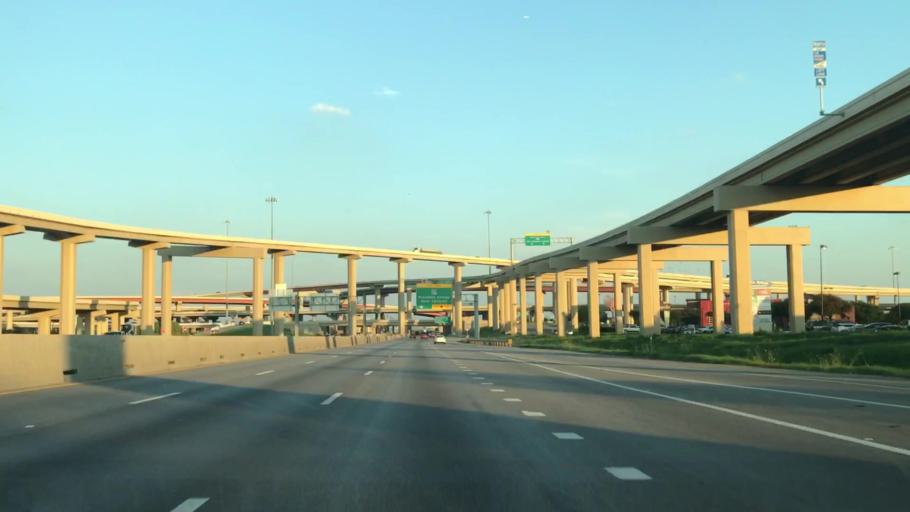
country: US
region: Texas
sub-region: Denton County
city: Lewisville
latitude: 33.0021
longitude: -96.9638
